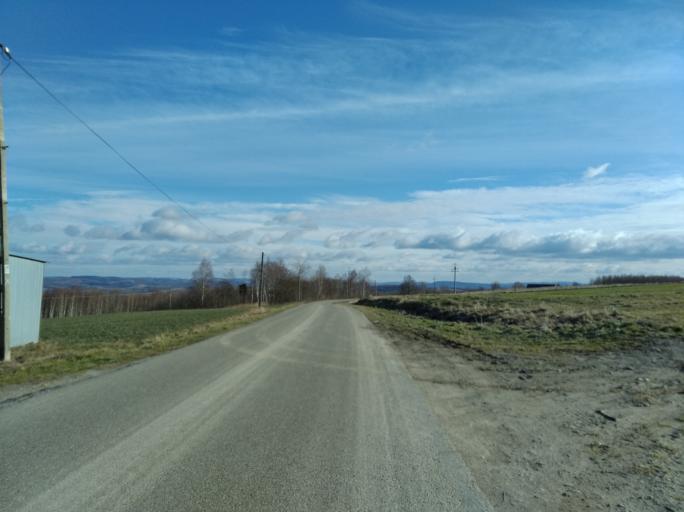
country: PL
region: Subcarpathian Voivodeship
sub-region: Powiat ropczycko-sedziszowski
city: Wielopole Skrzynskie
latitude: 49.9160
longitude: 21.6353
